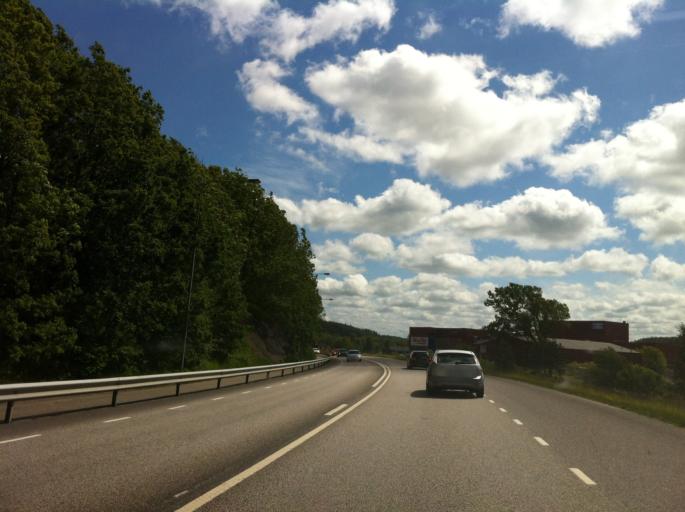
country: SE
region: Vaestra Goetaland
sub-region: Lilla Edets Kommun
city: Lilla Edet
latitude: 58.1129
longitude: 12.1429
